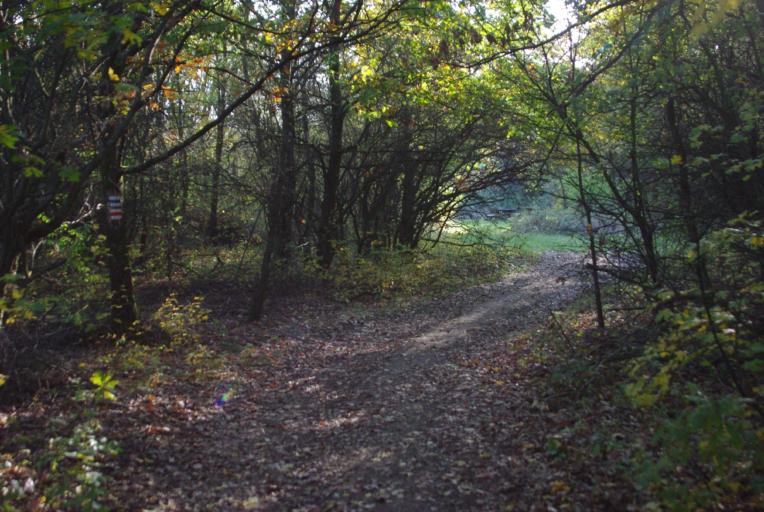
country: HU
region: Pest
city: Nagymaros
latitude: 47.8296
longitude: 18.9452
